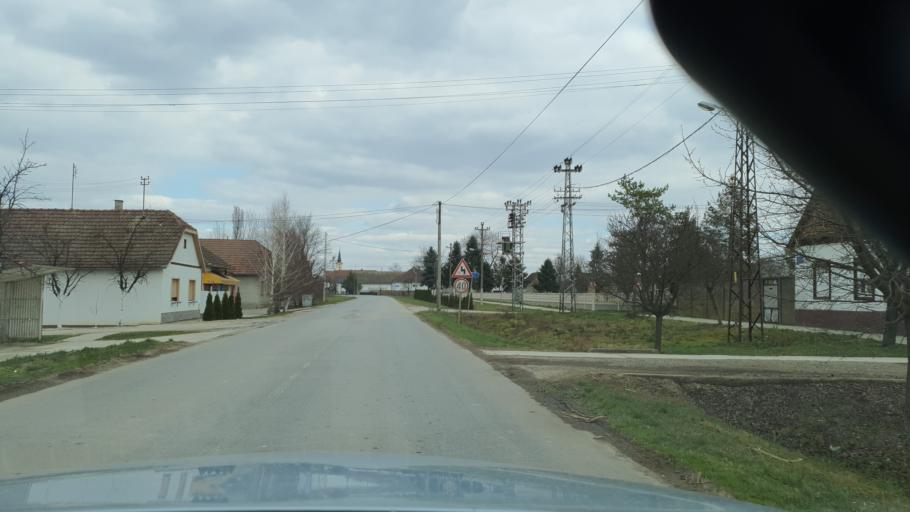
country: RS
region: Autonomna Pokrajina Vojvodina
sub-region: Juznobacki Okrug
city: Bac
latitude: 45.4047
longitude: 19.2888
